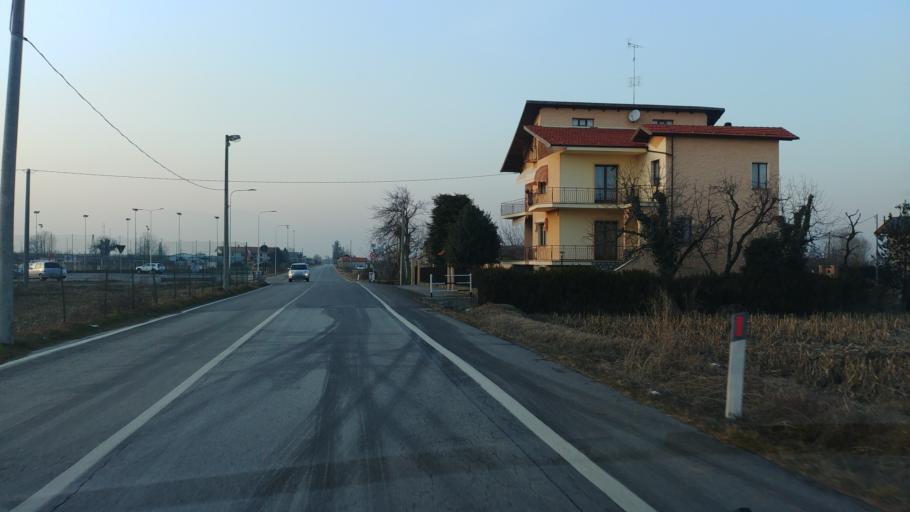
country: IT
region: Piedmont
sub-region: Provincia di Cuneo
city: Cuneo
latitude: 44.4170
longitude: 7.5373
